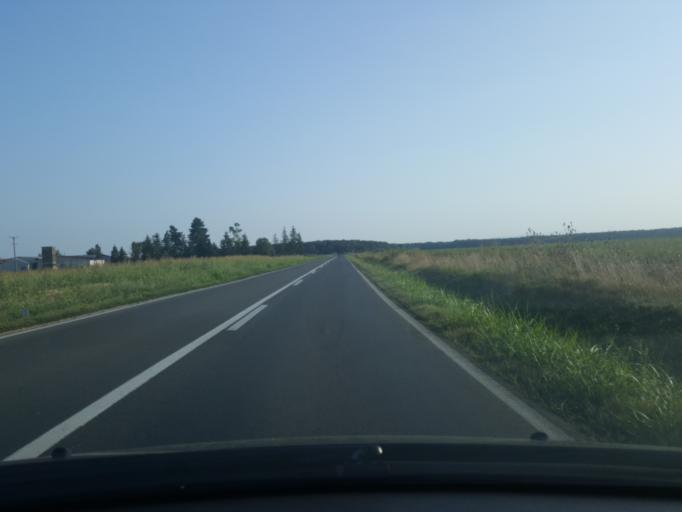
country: RS
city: Hrtkovci
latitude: 44.8514
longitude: 19.7707
